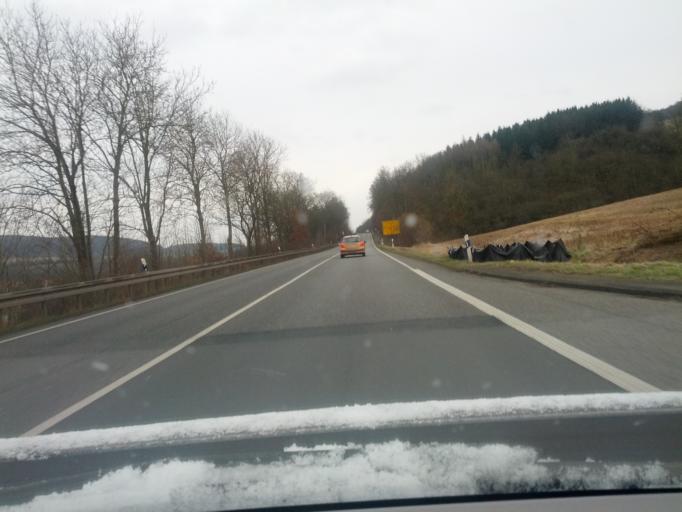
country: DE
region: Hesse
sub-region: Regierungsbezirk Kassel
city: Sontra
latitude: 51.1290
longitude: 9.9779
